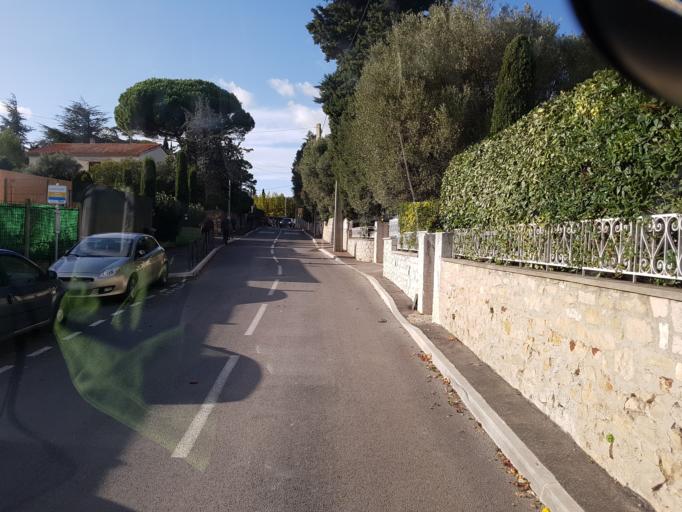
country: FR
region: Provence-Alpes-Cote d'Azur
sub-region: Departement des Bouches-du-Rhone
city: Cassis
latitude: 43.2123
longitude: 5.5437
